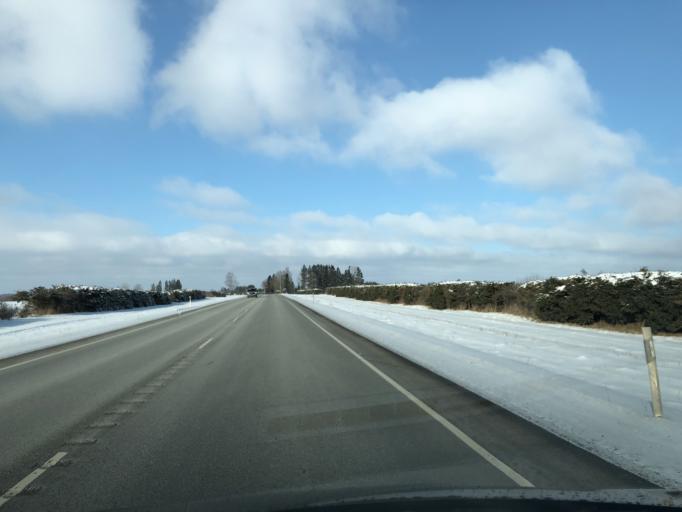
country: EE
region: Jaervamaa
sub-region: Paide linn
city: Paide
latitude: 58.8439
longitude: 25.7381
